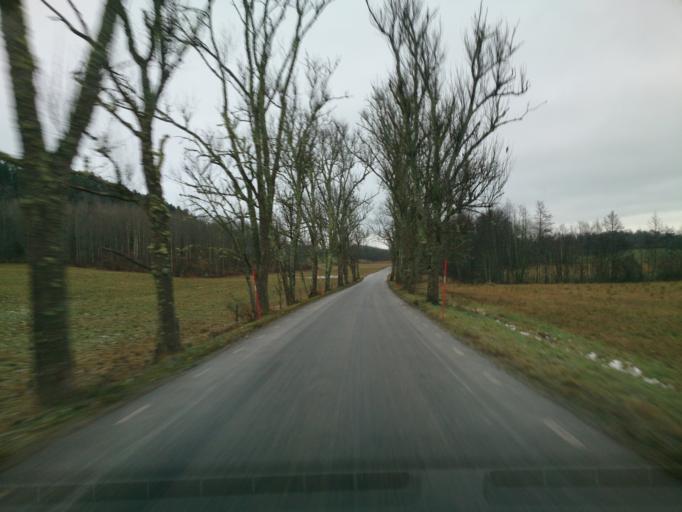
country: SE
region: OEstergoetland
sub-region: Atvidabergs Kommun
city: Atvidaberg
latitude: 58.2777
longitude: 16.1880
